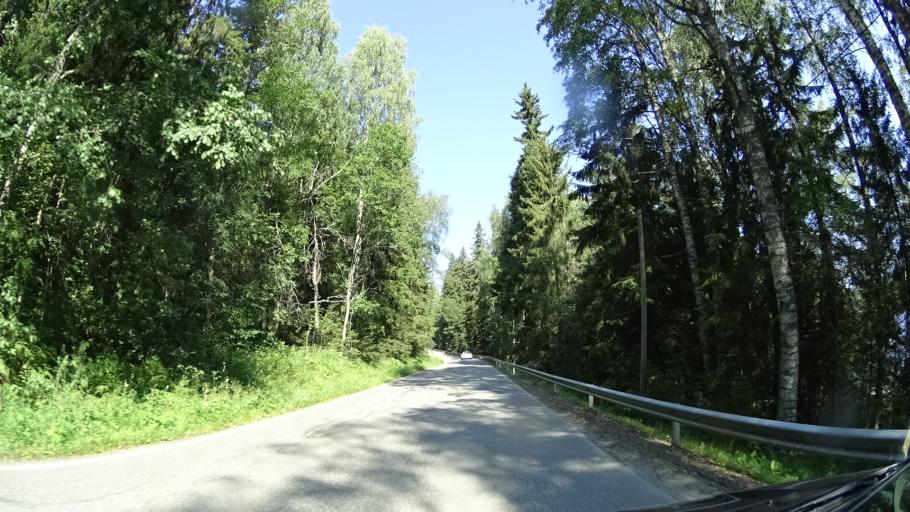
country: FI
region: North Karelia
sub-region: Pielisen Karjala
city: Lieksa
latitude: 63.1134
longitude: 29.8054
